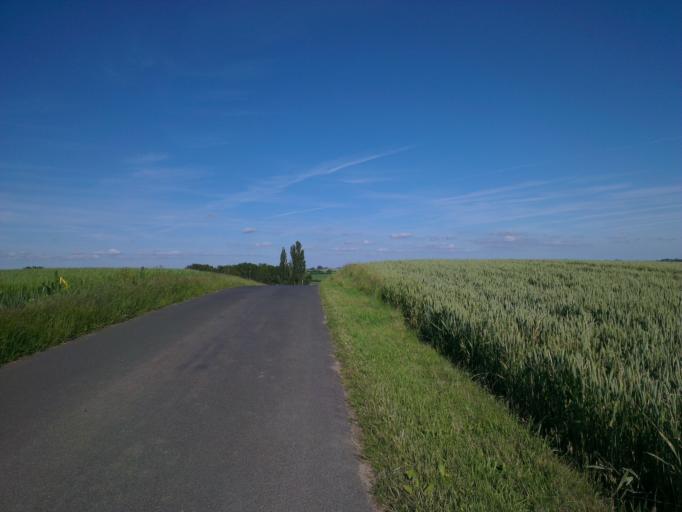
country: DK
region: Capital Region
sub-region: Frederikssund Kommune
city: Skibby
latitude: 55.7566
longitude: 11.9833
